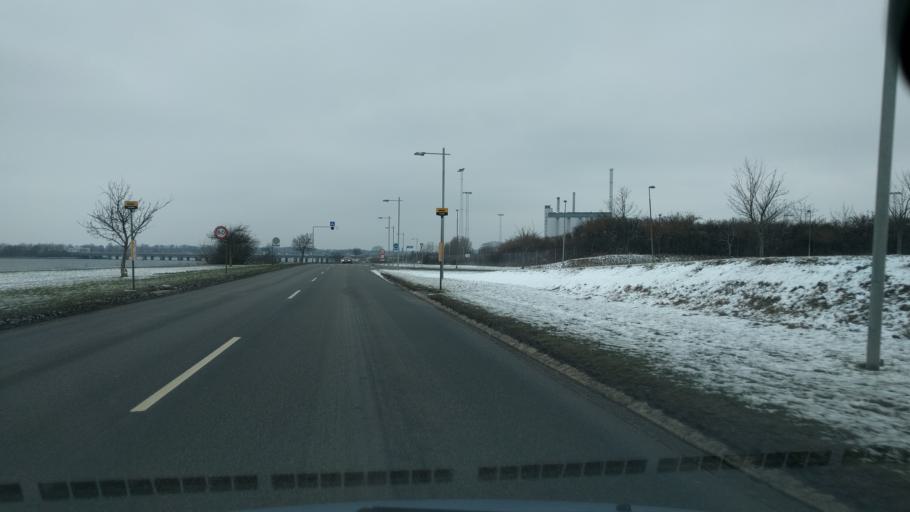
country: DK
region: Zealand
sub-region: Guldborgsund Kommune
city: Nykobing Falster
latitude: 54.7555
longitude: 11.8750
